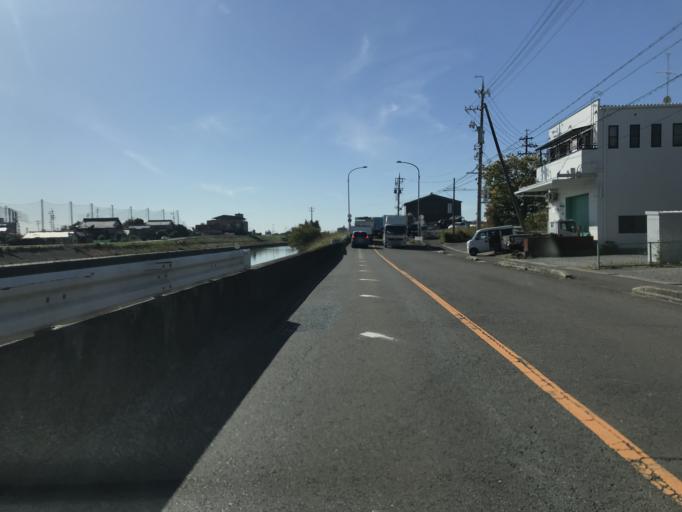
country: JP
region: Aichi
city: Nagoya-shi
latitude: 35.1871
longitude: 136.8463
